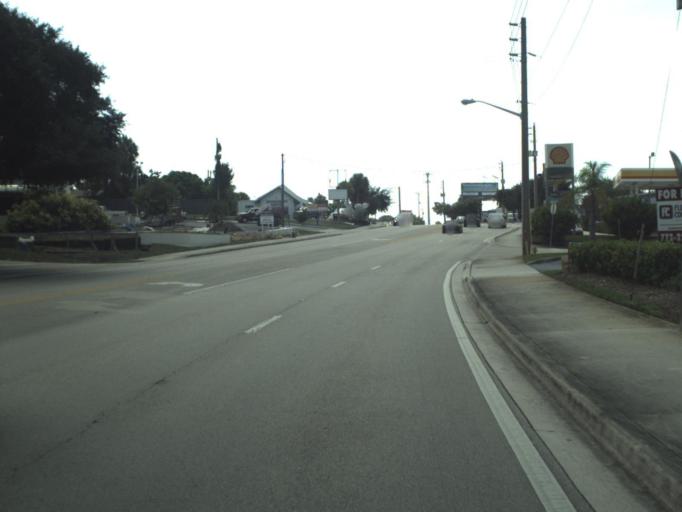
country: US
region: Florida
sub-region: Martin County
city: Jensen Beach
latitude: 27.2439
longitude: -80.2320
